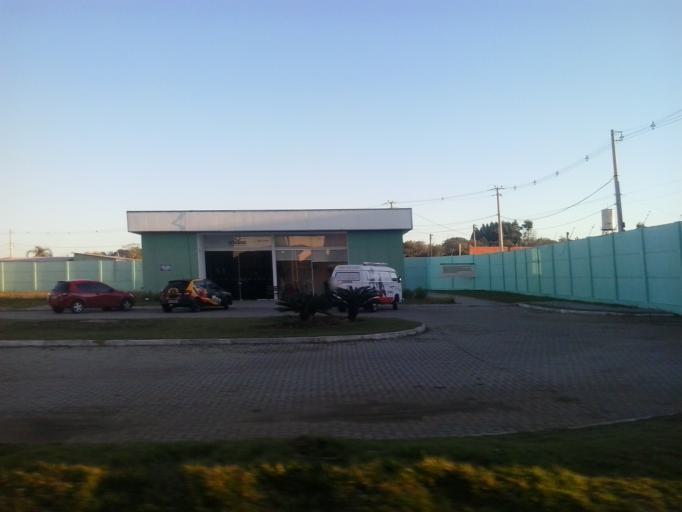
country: BR
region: Rio Grande do Sul
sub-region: Santa Maria
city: Santa Maria
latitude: -29.7002
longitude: -53.7286
